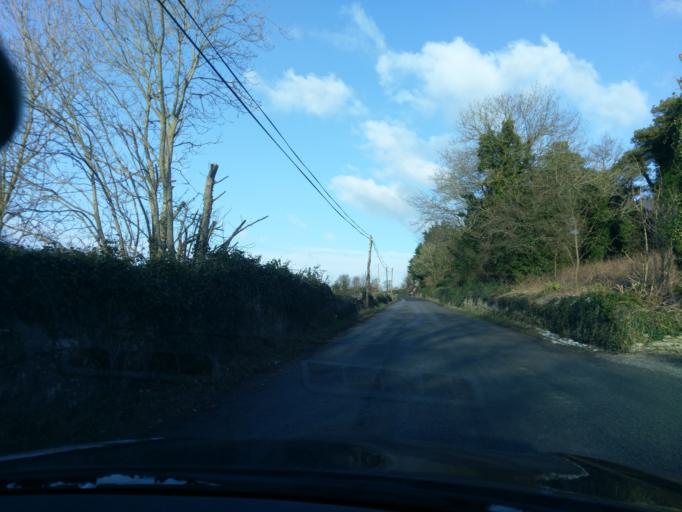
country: IE
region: Connaught
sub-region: County Galway
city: Gort
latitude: 53.1451
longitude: -8.7982
